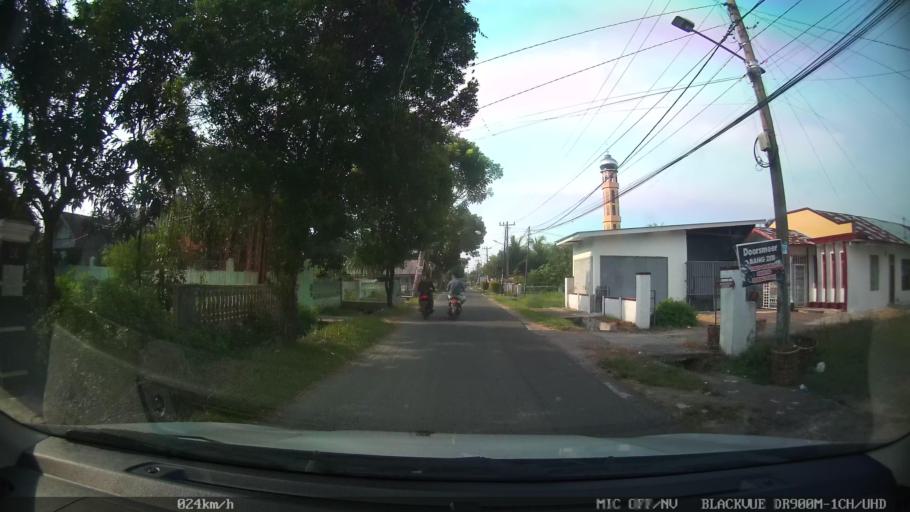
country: ID
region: North Sumatra
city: Binjai
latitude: 3.6052
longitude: 98.5114
